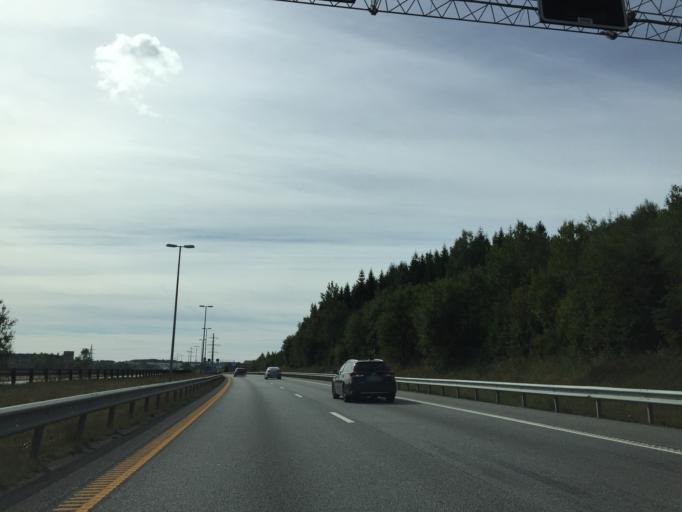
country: NO
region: Akershus
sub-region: Vestby
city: Vestby
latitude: 59.6139
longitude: 10.7322
